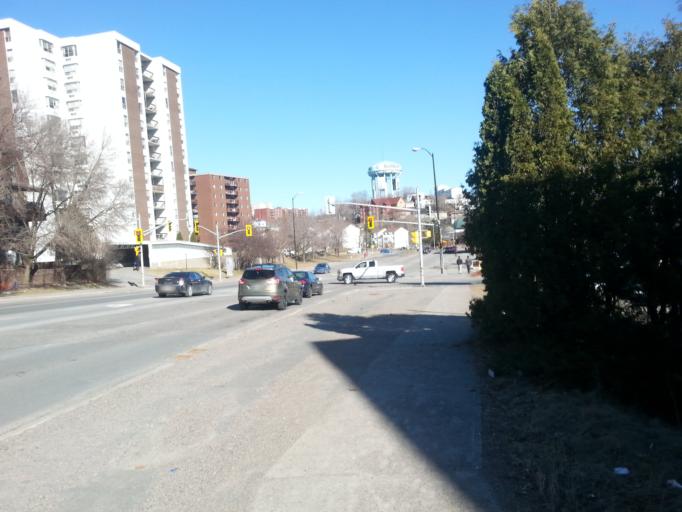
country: CA
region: Ontario
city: Greater Sudbury
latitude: 46.4954
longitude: -80.9938
